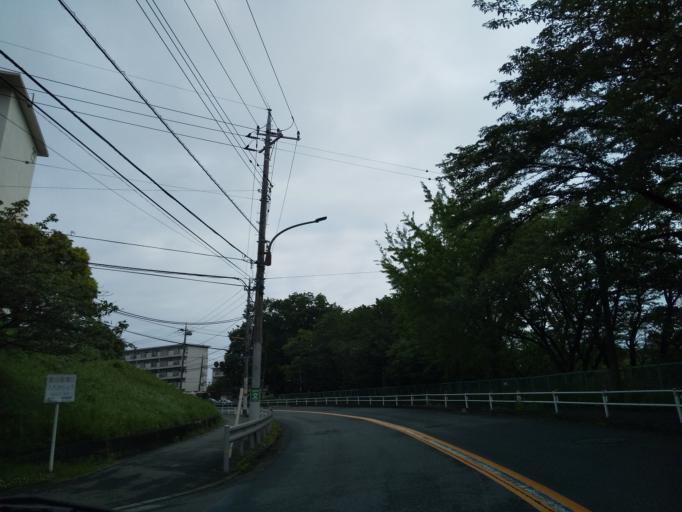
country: JP
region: Tokyo
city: Hino
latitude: 35.6529
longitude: 139.4164
